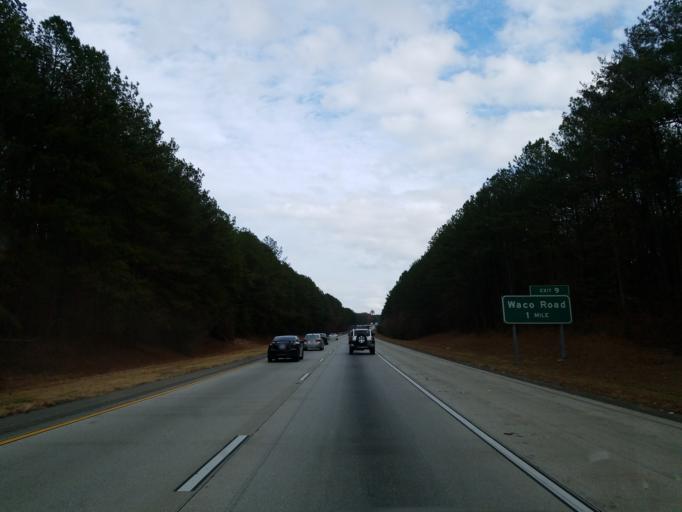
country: US
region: Georgia
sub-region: Carroll County
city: Mount Zion
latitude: 33.6890
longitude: -85.2092
